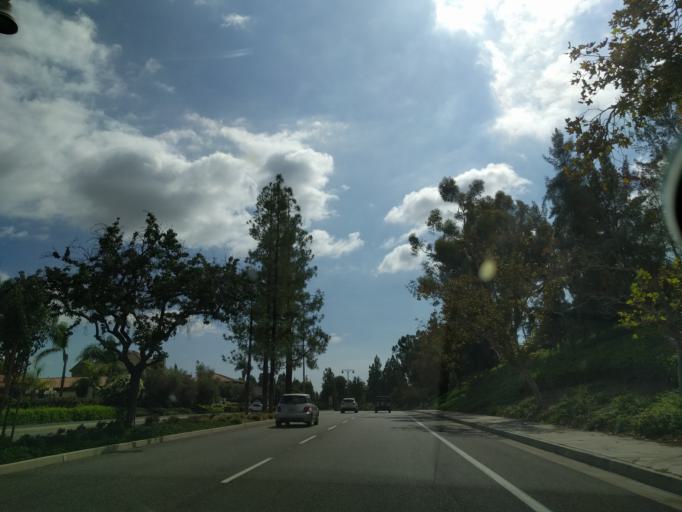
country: US
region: California
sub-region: Orange County
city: Mission Viejo
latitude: 33.6321
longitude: -117.6491
